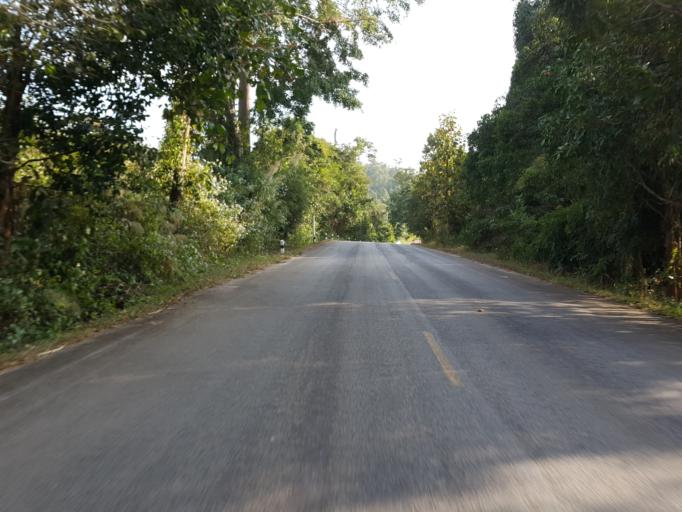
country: TH
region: Lamphun
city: Thung Hua Chang
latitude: 18.1111
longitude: 99.0164
